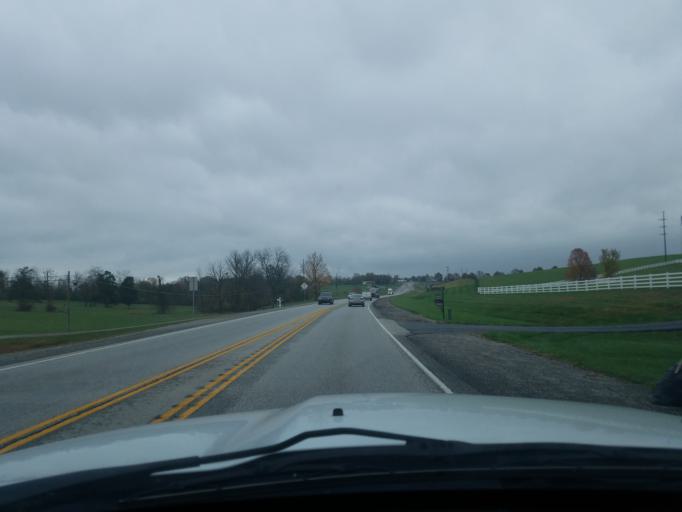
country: US
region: Kentucky
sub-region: Marion County
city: Lebanon
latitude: 37.5525
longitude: -85.2933
